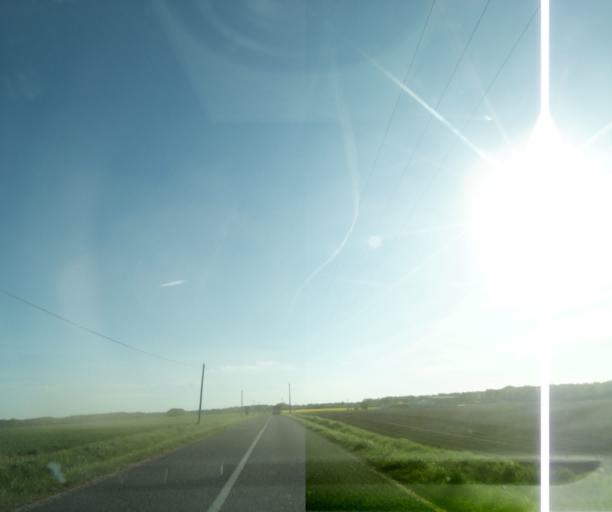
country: FR
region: Ile-de-France
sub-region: Departement de Seine-et-Marne
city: Nangis
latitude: 48.5500
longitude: 3.0000
